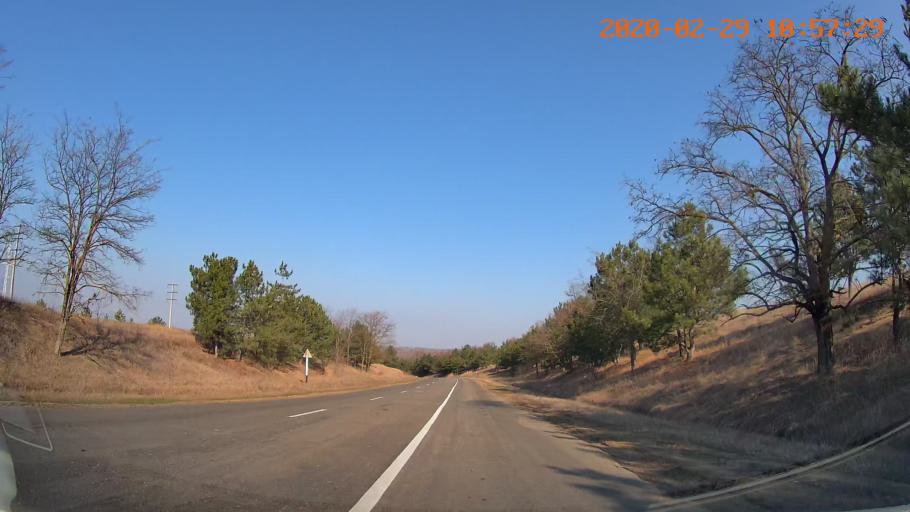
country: MD
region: Telenesti
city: Grigoriopol
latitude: 47.1599
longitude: 29.3219
